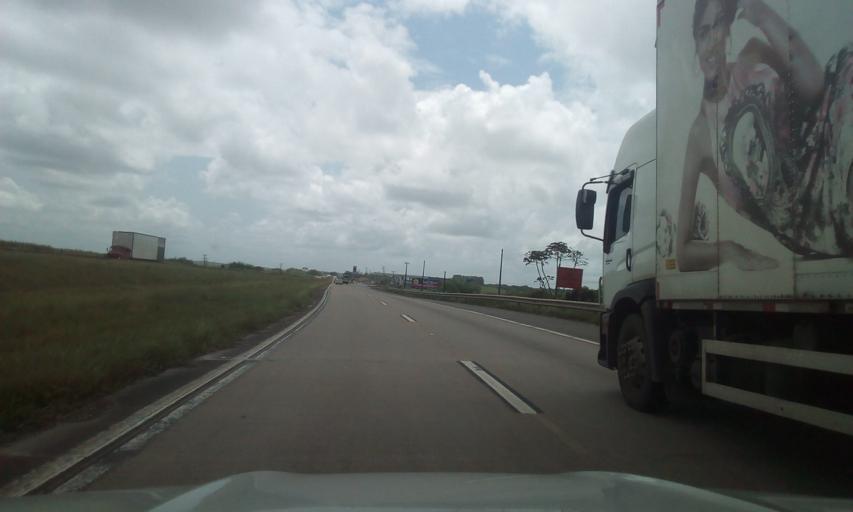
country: BR
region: Pernambuco
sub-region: Goiana
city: Goiana
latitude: -7.6599
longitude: -34.9377
